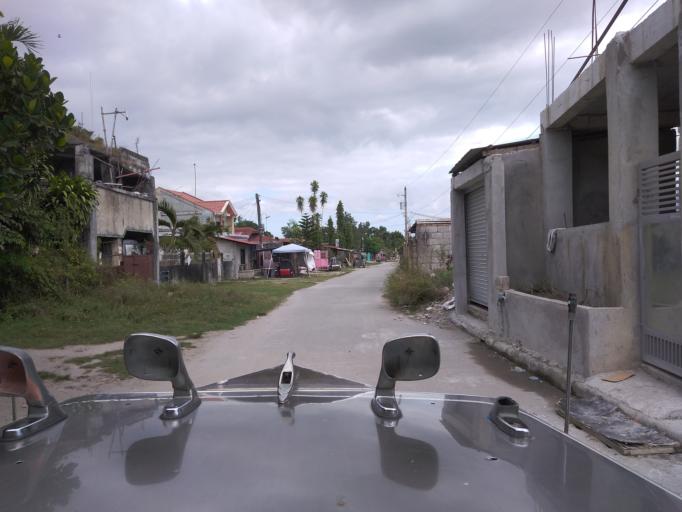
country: PH
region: Central Luzon
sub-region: Province of Pampanga
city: Pandacaqui
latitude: 15.1880
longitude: 120.6479
